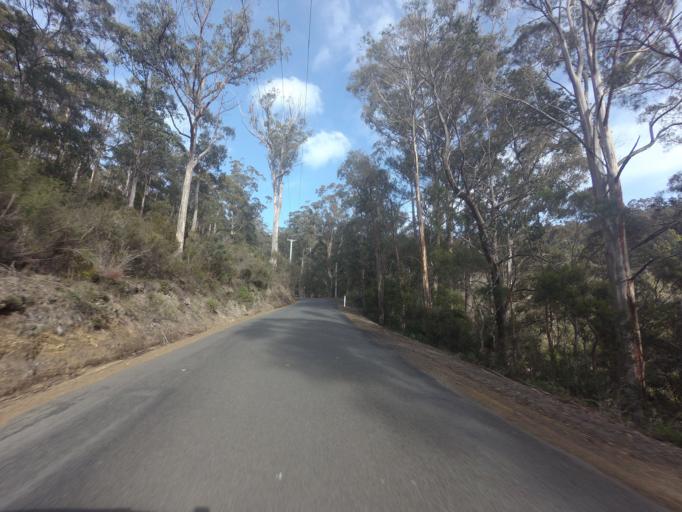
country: AU
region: Tasmania
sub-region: Kingborough
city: Margate
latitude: -43.0061
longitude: 147.1699
